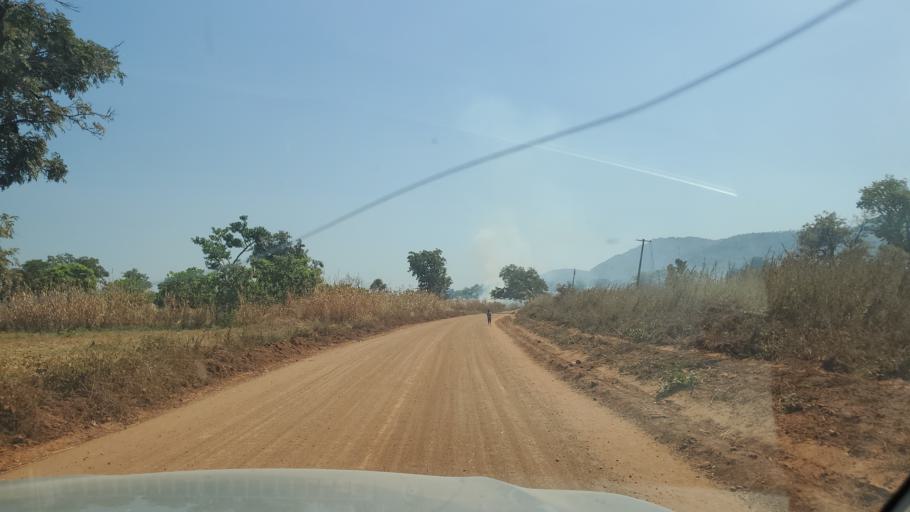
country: NG
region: Niger
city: Gawu Babangida
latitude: 9.2201
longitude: 6.8413
